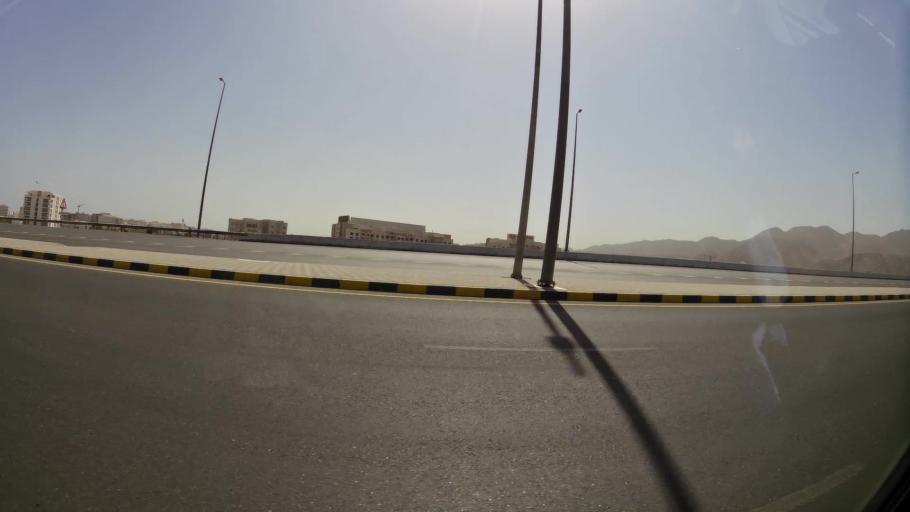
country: OM
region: Muhafazat Masqat
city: Bawshar
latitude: 23.5853
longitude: 58.4159
